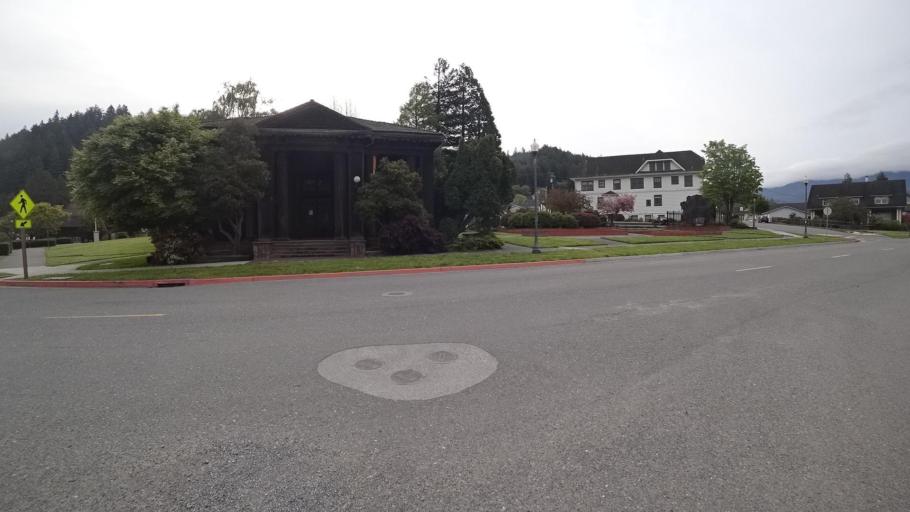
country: US
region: California
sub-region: Humboldt County
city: Rio Dell
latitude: 40.4837
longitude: -124.1028
